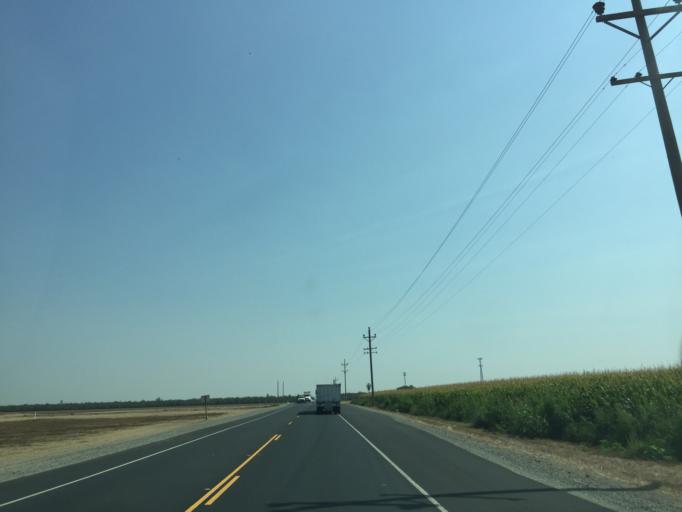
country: US
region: California
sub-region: Kings County
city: Lucerne
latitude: 36.4149
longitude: -119.6368
